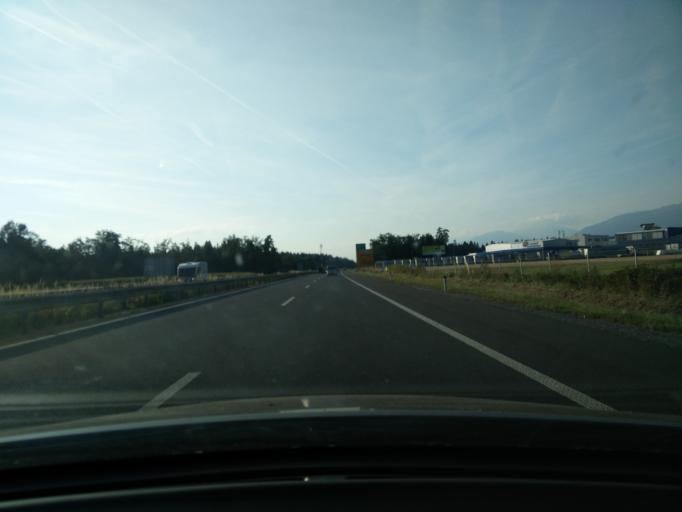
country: SI
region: Sencur
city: Sencur
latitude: 46.2326
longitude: 14.4120
